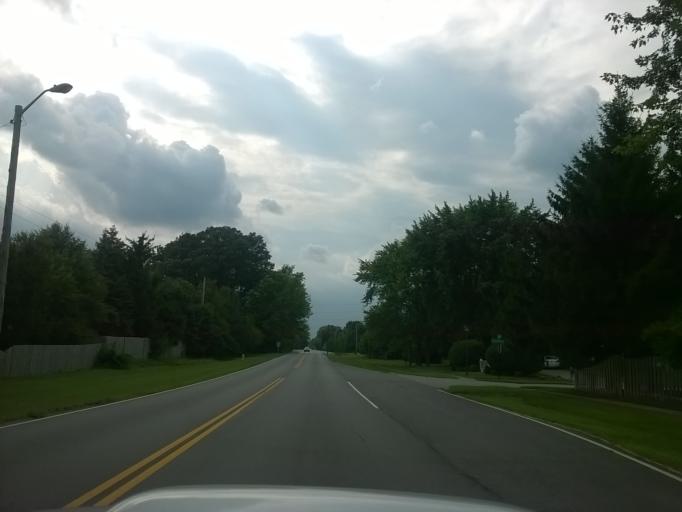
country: US
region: Indiana
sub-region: Hamilton County
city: Carmel
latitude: 39.9784
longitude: -86.0929
